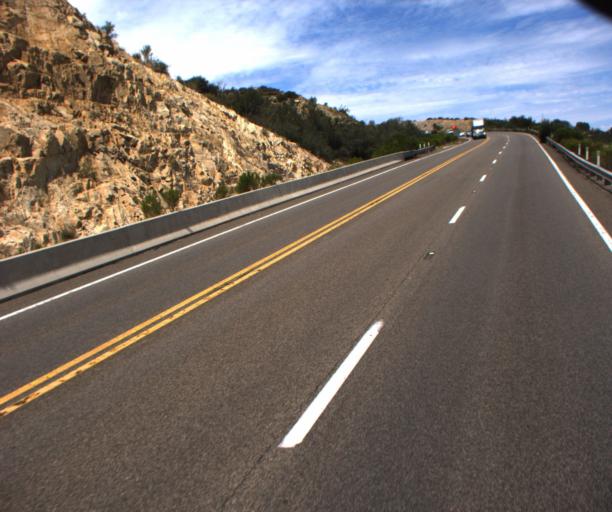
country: US
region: Arizona
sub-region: Gila County
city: Miami
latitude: 33.3640
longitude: -110.9603
